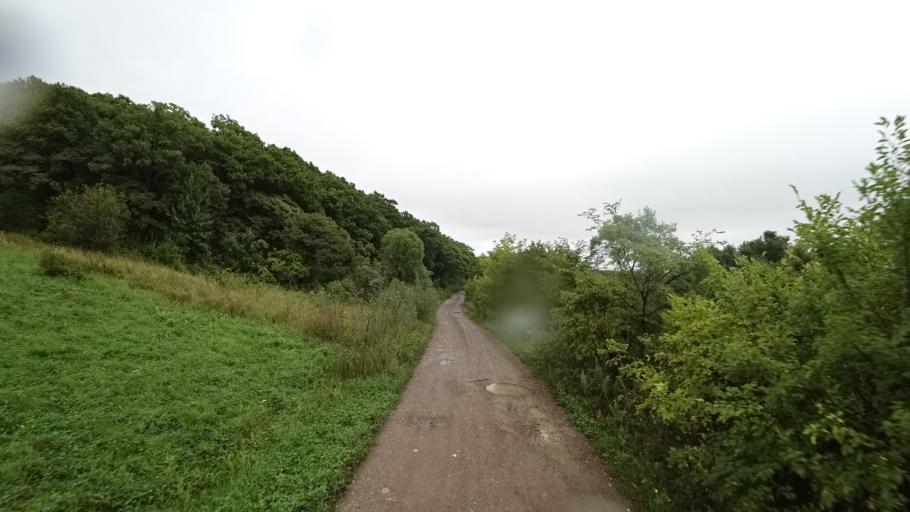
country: RU
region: Primorskiy
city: Monastyrishche
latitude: 44.2614
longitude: 132.4061
